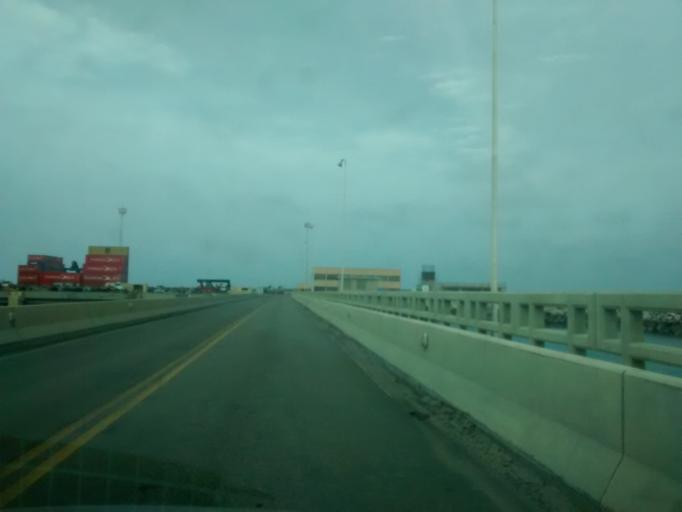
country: BR
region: Ceara
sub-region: Caucaia
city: Cambebba
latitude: -3.5323
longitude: -38.7947
